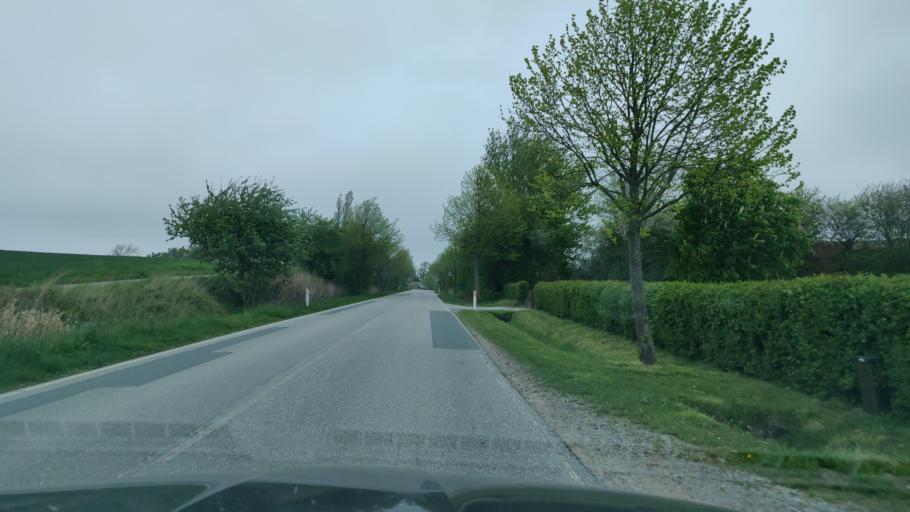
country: DK
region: South Denmark
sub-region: Sonderborg Kommune
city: Guderup
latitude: 54.9901
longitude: 9.8885
